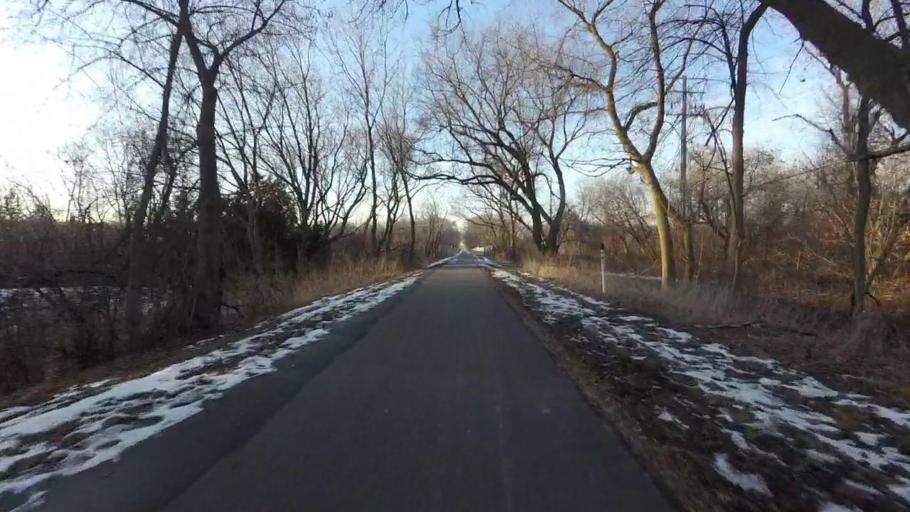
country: US
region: Wisconsin
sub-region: Milwaukee County
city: Whitefish Bay
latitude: 43.1127
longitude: -87.9221
